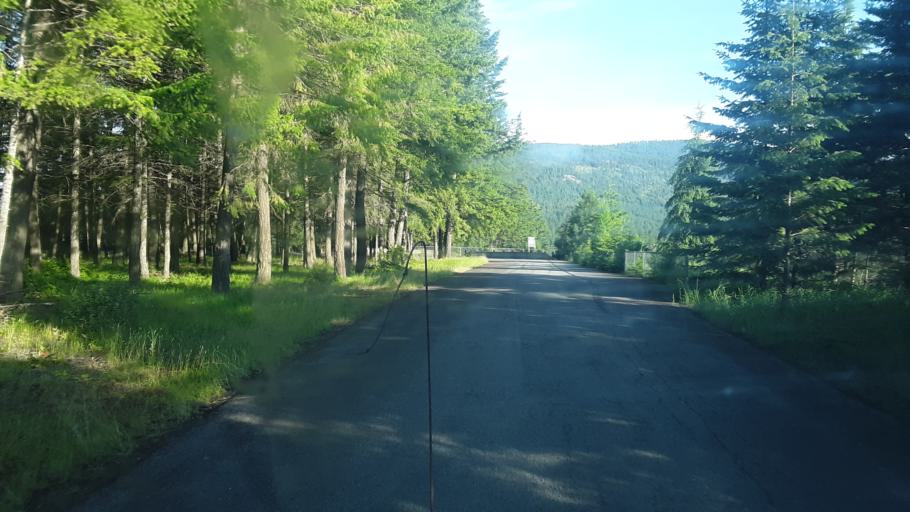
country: US
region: Idaho
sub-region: Boundary County
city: Bonners Ferry
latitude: 48.7264
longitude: -116.1756
